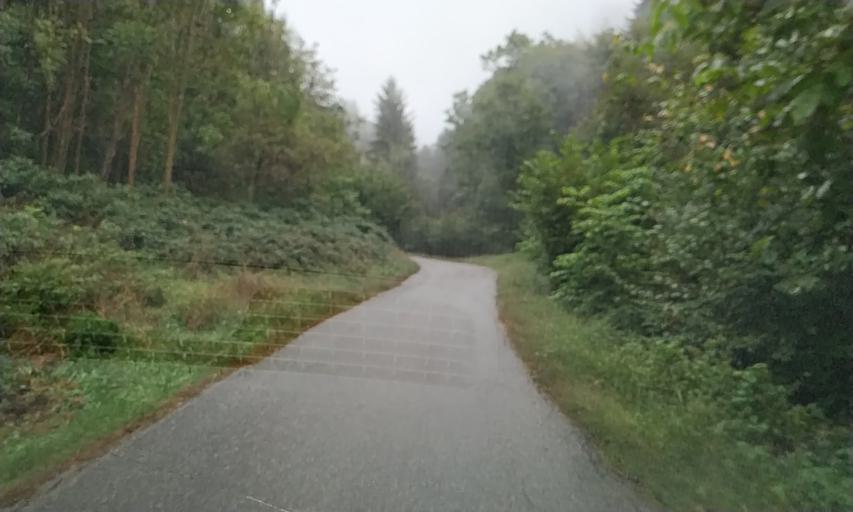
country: IT
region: Piedmont
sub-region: Provincia di Vercelli
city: Civiasco
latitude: 45.8314
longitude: 8.2892
